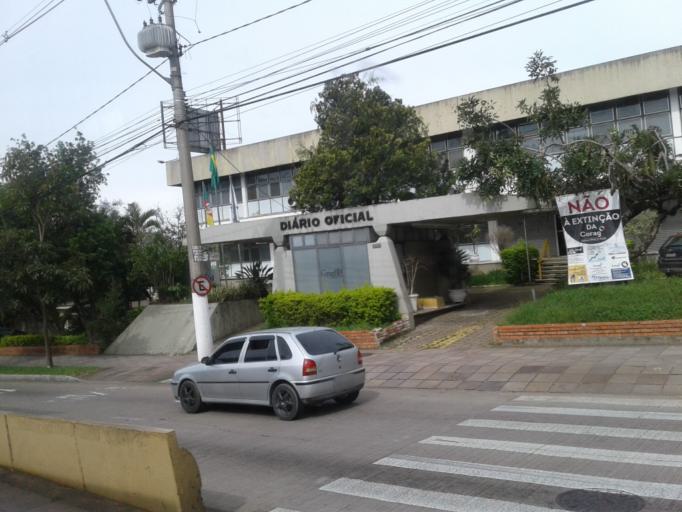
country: BR
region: Rio Grande do Sul
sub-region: Porto Alegre
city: Porto Alegre
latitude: -30.0688
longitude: -51.1880
